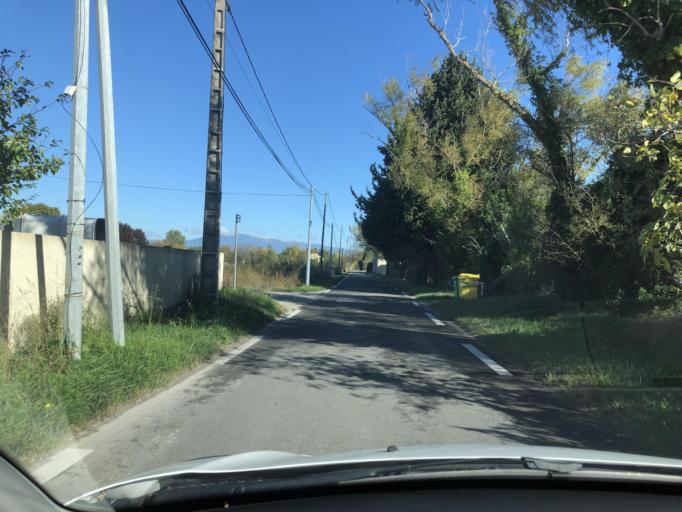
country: FR
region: Provence-Alpes-Cote d'Azur
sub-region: Departement du Vaucluse
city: Althen-des-Paluds
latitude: 43.9841
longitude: 4.9576
